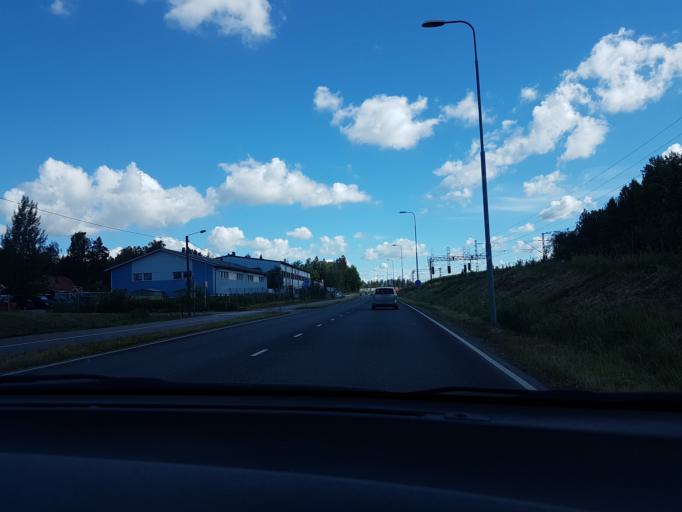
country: FI
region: Uusimaa
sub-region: Helsinki
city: Kerava
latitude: 60.3697
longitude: 25.0920
